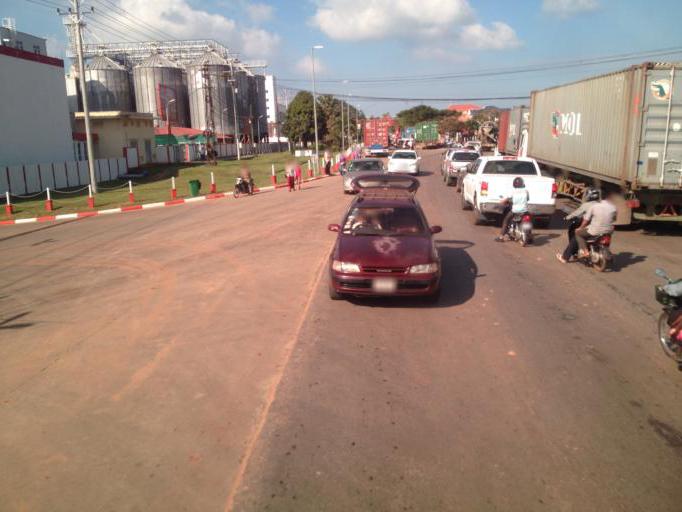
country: KH
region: Preah Sihanouk
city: Sihanoukville
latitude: 10.6348
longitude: 103.5359
